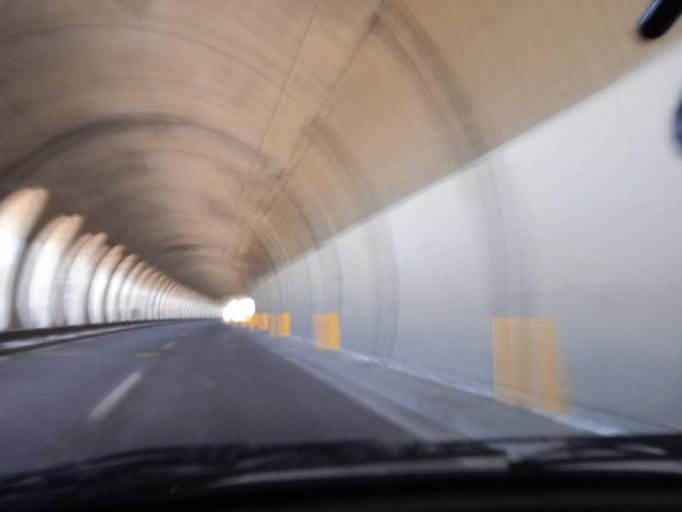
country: IT
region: Sicily
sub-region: Messina
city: Naso
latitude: 38.1500
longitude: 14.7669
